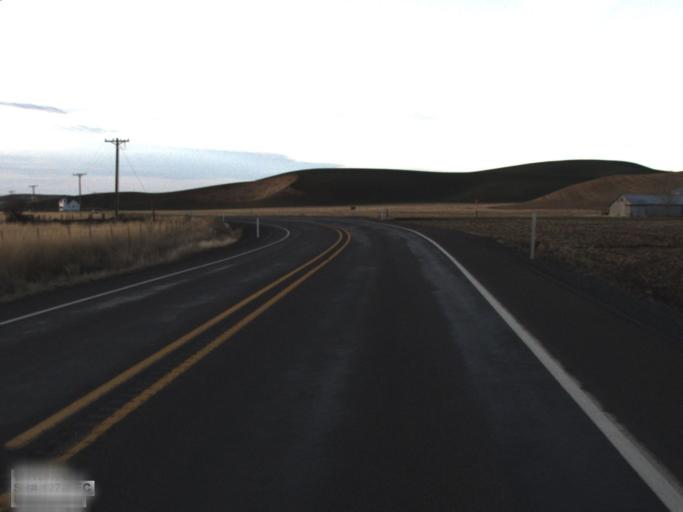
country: US
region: Washington
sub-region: Garfield County
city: Pomeroy
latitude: 46.7848
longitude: -117.6989
